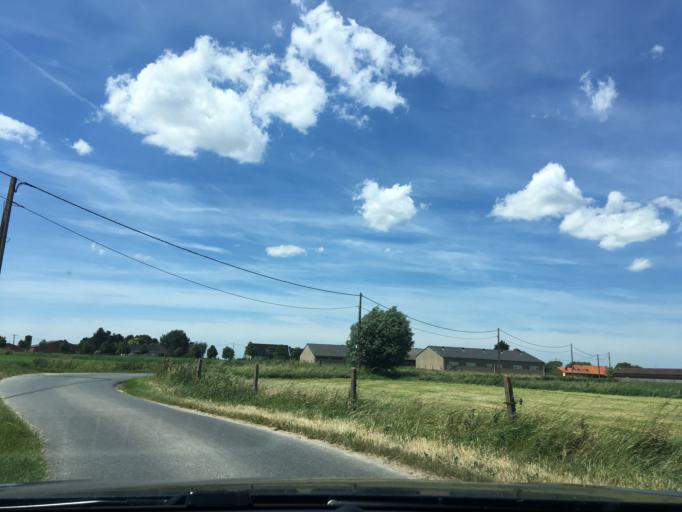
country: BE
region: Flanders
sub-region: Provincie West-Vlaanderen
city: Lichtervelde
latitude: 51.0211
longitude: 3.1853
